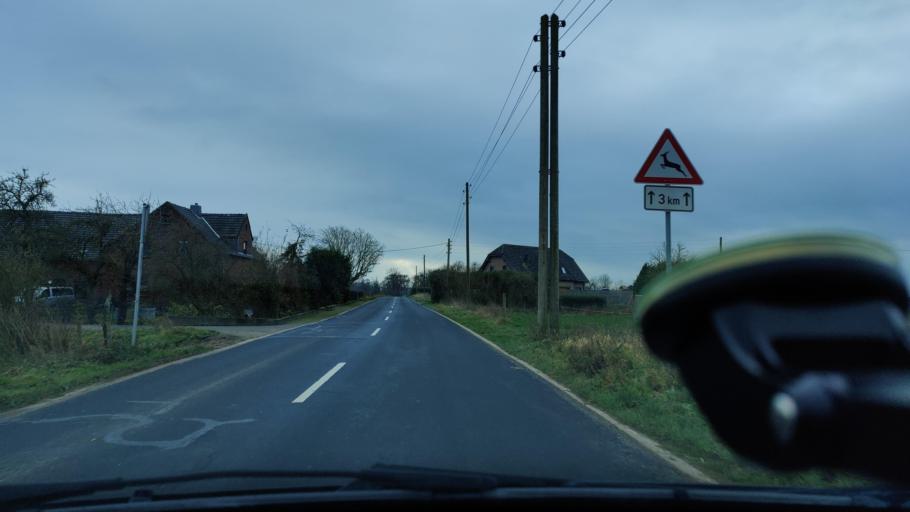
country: DE
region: North Rhine-Westphalia
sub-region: Regierungsbezirk Dusseldorf
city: Alpen
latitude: 51.6113
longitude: 6.4765
